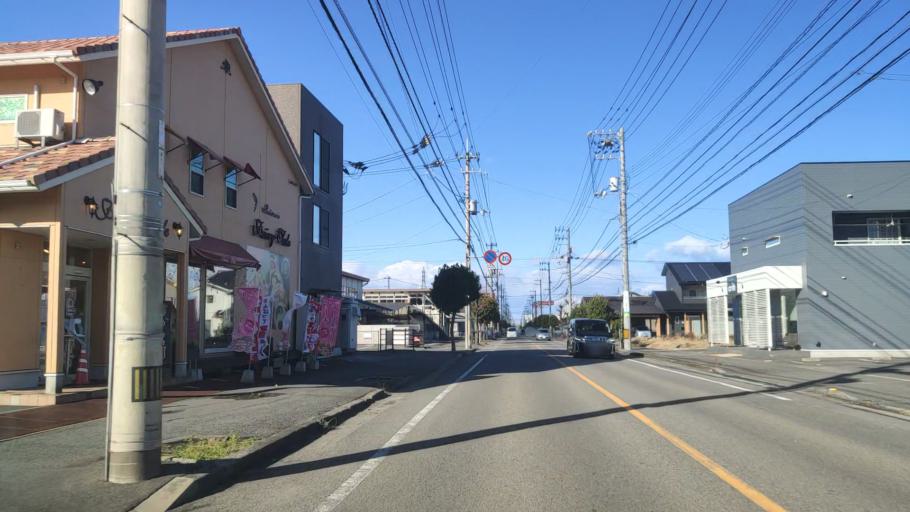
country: JP
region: Ehime
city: Saijo
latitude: 33.9224
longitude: 133.1916
